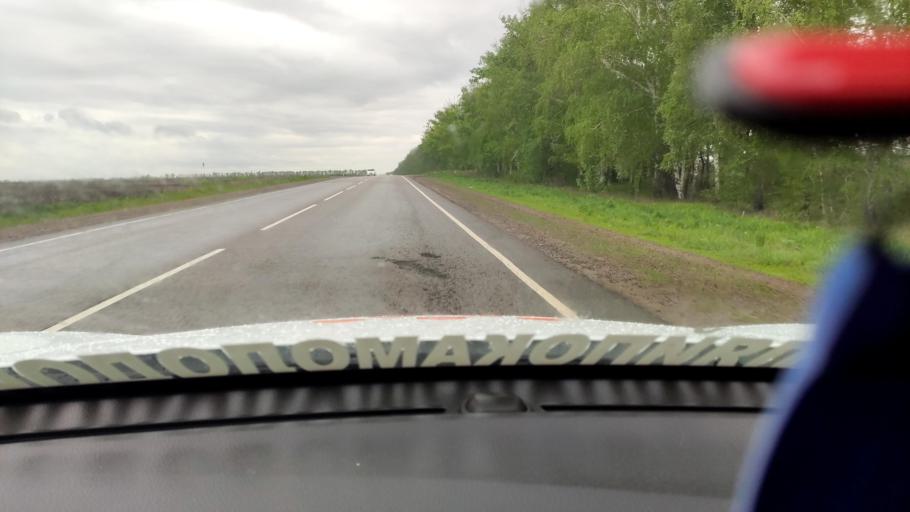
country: RU
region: Voronezj
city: Sredniy Ikorets
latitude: 51.0407
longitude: 39.6771
